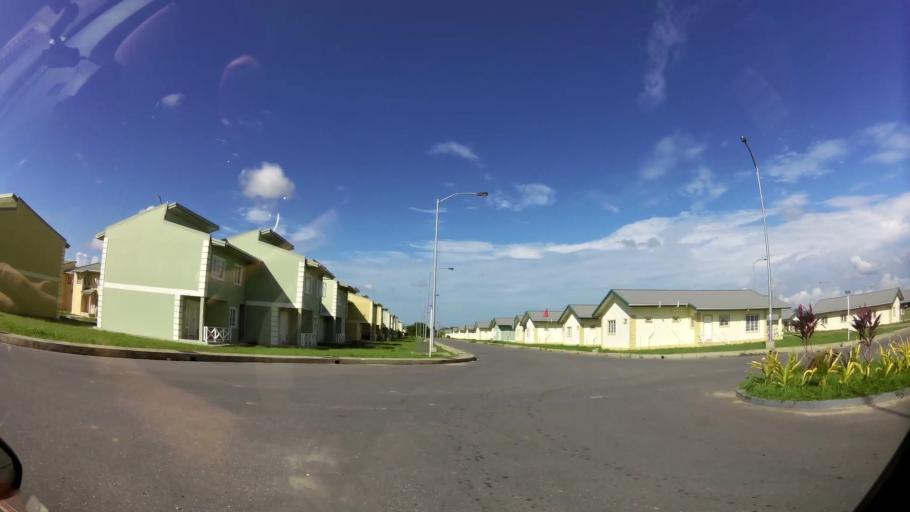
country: TT
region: Chaguanas
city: Chaguanas
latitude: 10.5332
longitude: -61.3940
